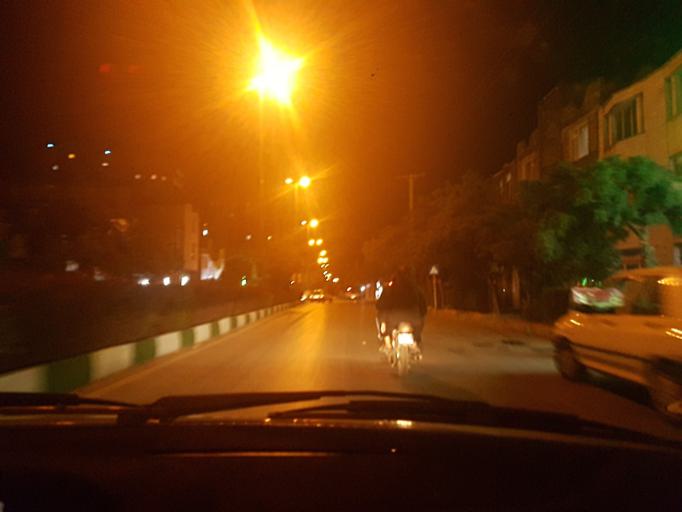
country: IR
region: Markazi
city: Arak
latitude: 34.0710
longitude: 49.6763
